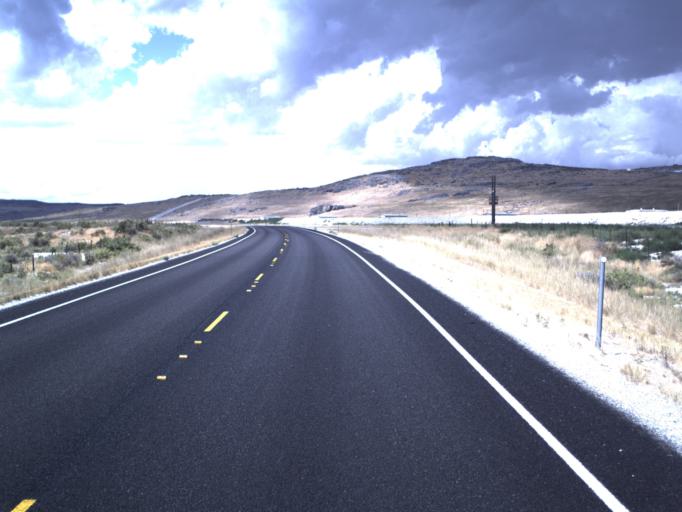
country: US
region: Utah
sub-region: Box Elder County
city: Tremonton
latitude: 41.6242
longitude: -112.3923
